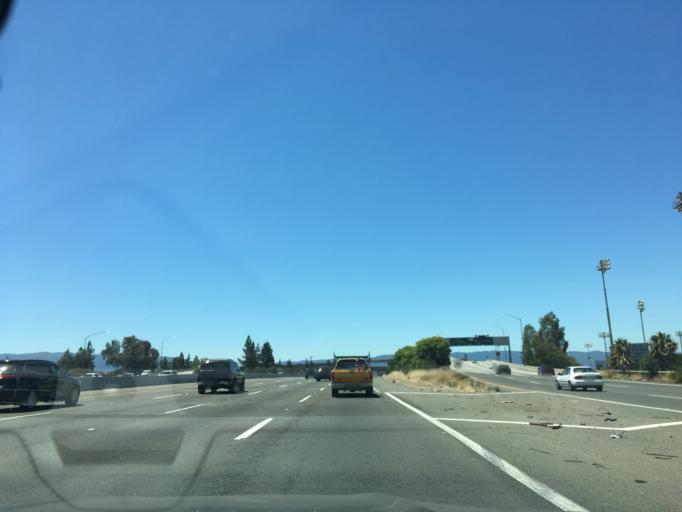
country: US
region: California
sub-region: Santa Clara County
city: Alum Rock
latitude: 37.3434
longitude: -121.8466
